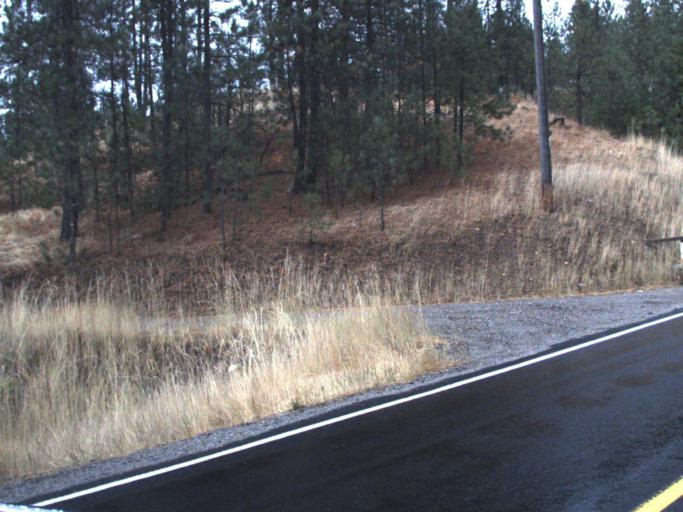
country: US
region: Washington
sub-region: Spokane County
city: Deer Park
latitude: 48.0130
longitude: -117.7313
